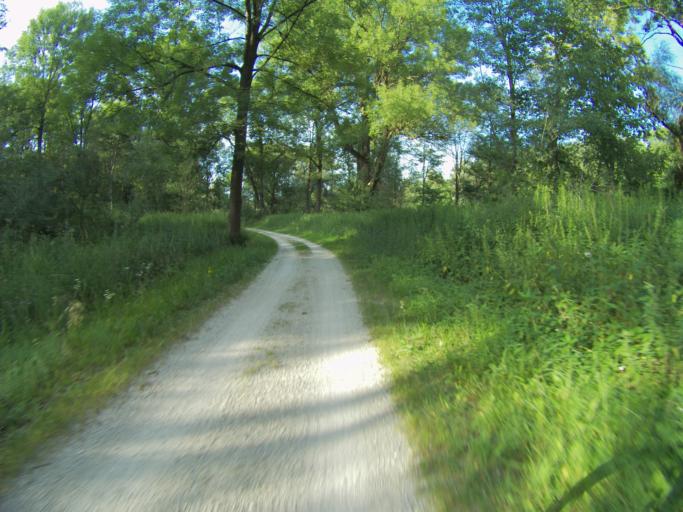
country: DE
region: Bavaria
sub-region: Upper Bavaria
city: Hallbergmoos
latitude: 48.3348
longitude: 11.7134
